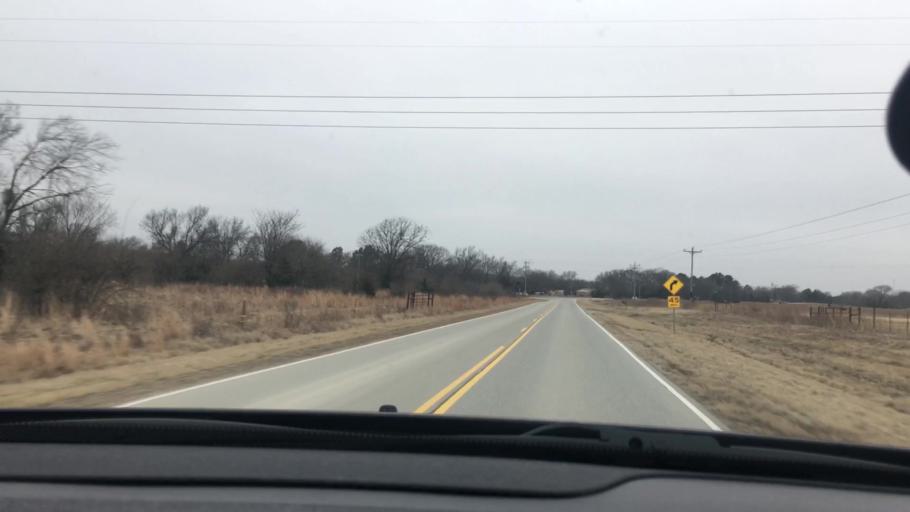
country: US
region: Oklahoma
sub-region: Coal County
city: Coalgate
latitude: 34.5072
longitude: -96.2999
